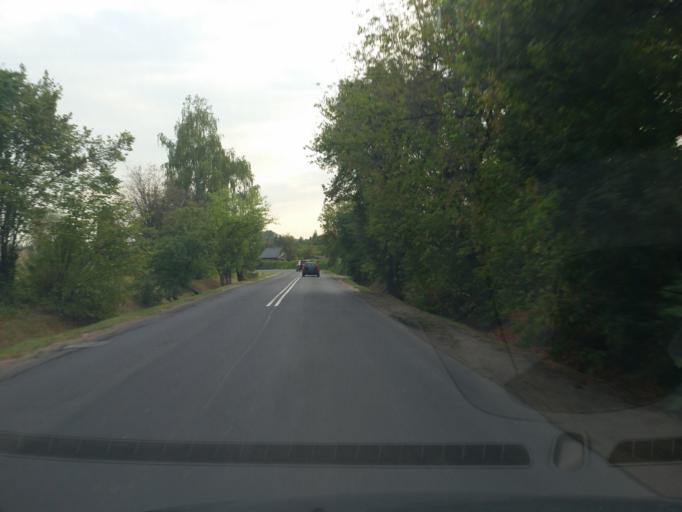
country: PL
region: Masovian Voivodeship
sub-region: Warszawa
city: Wlochy
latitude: 52.1758
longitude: 20.9838
